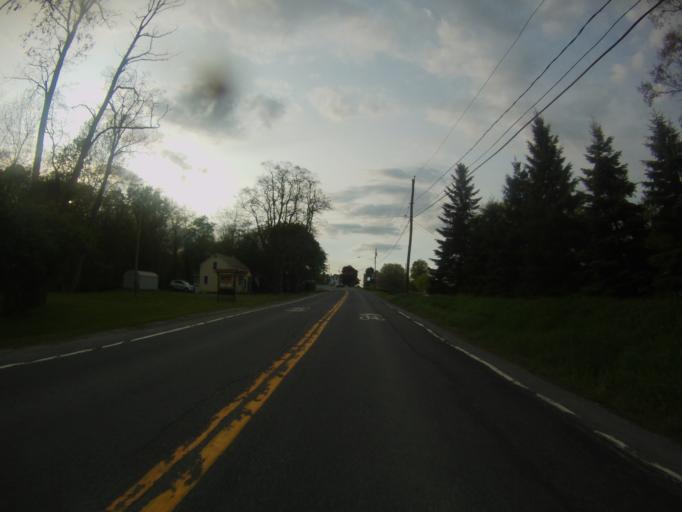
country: US
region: New York
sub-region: Essex County
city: Ticonderoga
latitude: 43.9491
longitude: -73.4183
